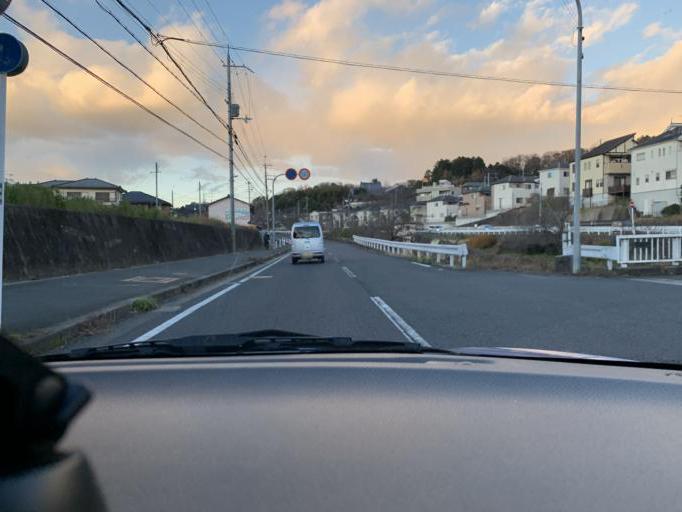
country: JP
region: Nara
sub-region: Ikoma-shi
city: Ikoma
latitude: 34.7024
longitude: 135.7333
